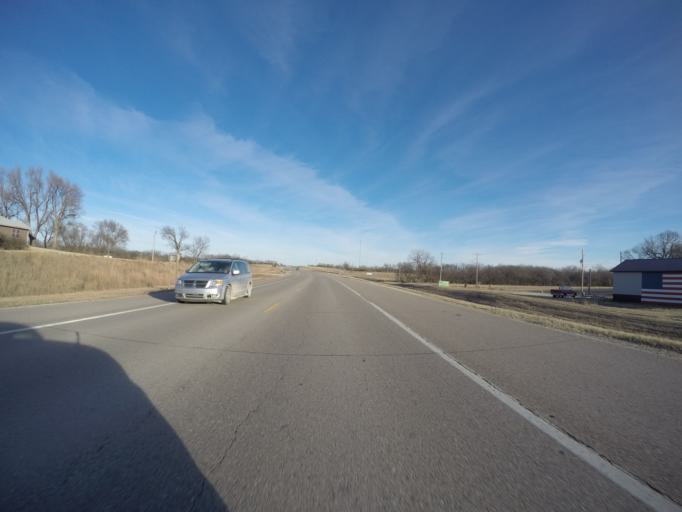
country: US
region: Kansas
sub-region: Marion County
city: Peabody
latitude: 38.1752
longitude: -97.1016
